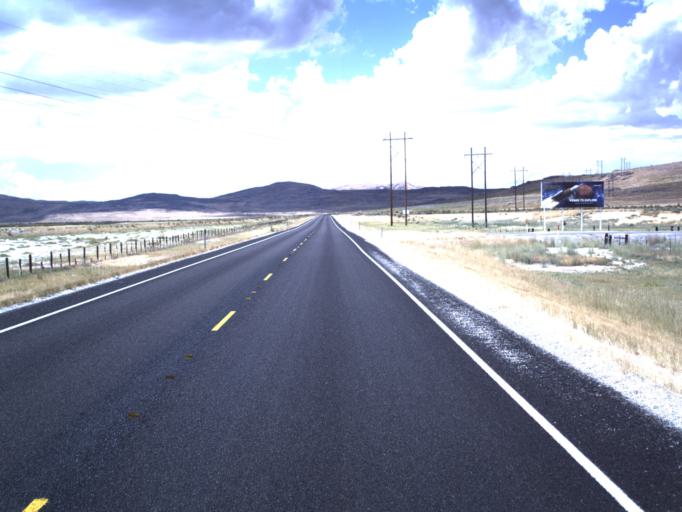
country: US
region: Utah
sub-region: Box Elder County
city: Tremonton
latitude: 41.6281
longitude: -112.4052
